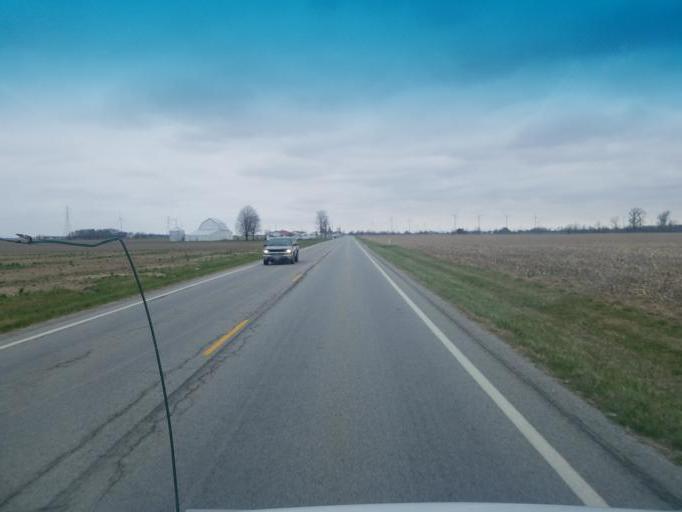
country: US
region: Ohio
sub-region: Van Wert County
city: Van Wert
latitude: 40.9320
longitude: -84.4844
